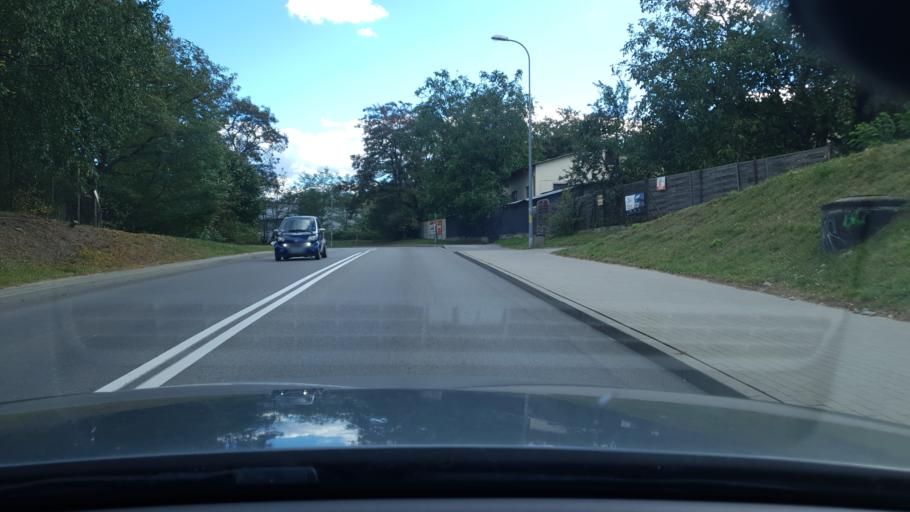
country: PL
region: Pomeranian Voivodeship
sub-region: Powiat wejherowski
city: Reda
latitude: 54.6005
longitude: 18.3447
